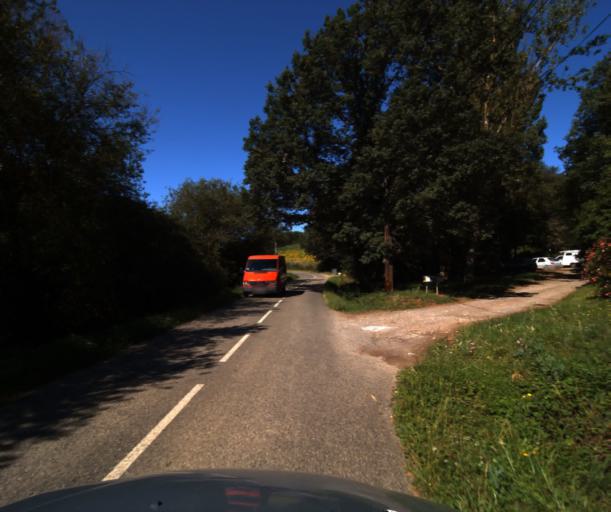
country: FR
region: Midi-Pyrenees
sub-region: Departement de la Haute-Garonne
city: Eaunes
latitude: 43.4197
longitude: 1.3447
